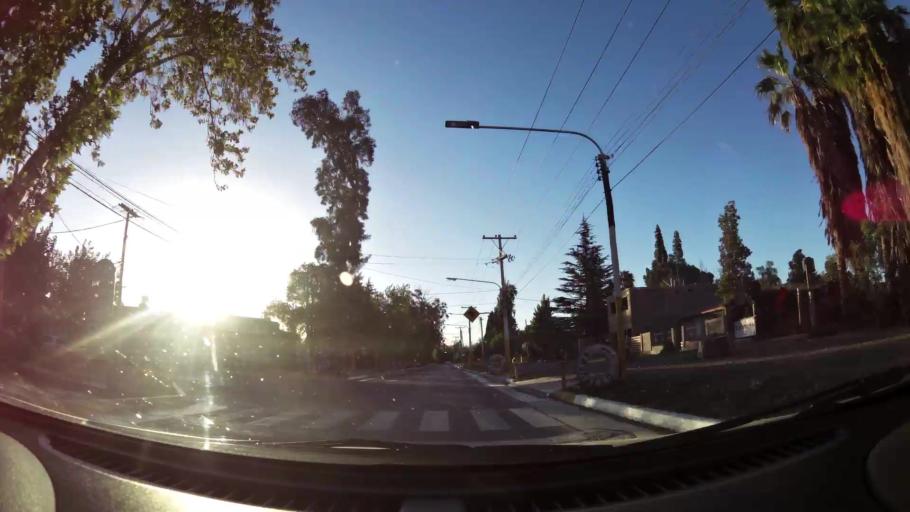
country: AR
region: San Juan
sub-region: Departamento de Santa Lucia
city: Santa Lucia
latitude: -31.5458
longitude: -68.4816
